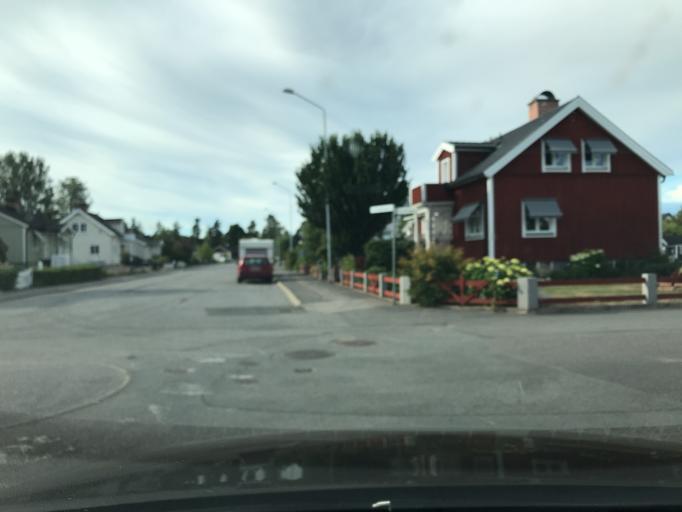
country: SE
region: Kalmar
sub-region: Hultsfreds Kommun
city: Hultsfred
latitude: 57.4984
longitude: 15.8492
